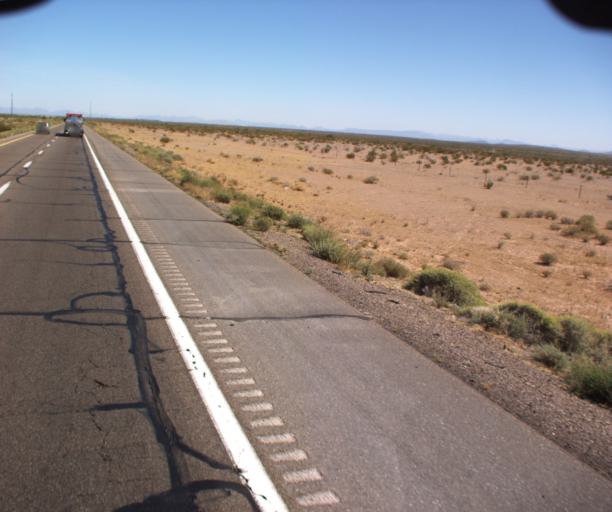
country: US
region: Arizona
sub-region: Maricopa County
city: Gila Bend
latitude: 32.8994
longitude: -113.0132
